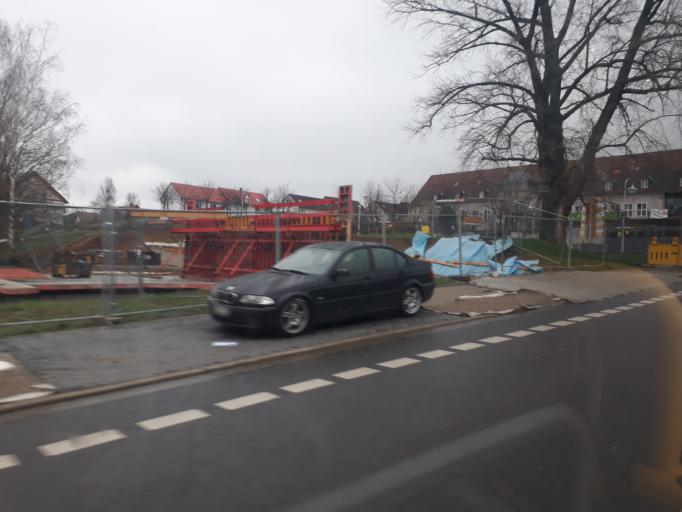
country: DE
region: Saxony
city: Kreischa
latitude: 50.9905
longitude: 13.7965
